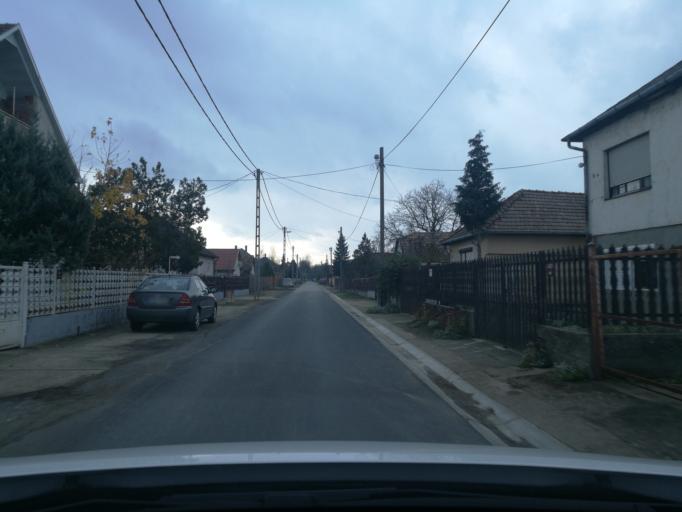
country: HU
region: Szabolcs-Szatmar-Bereg
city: Nyirpazony
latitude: 47.9790
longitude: 21.7878
